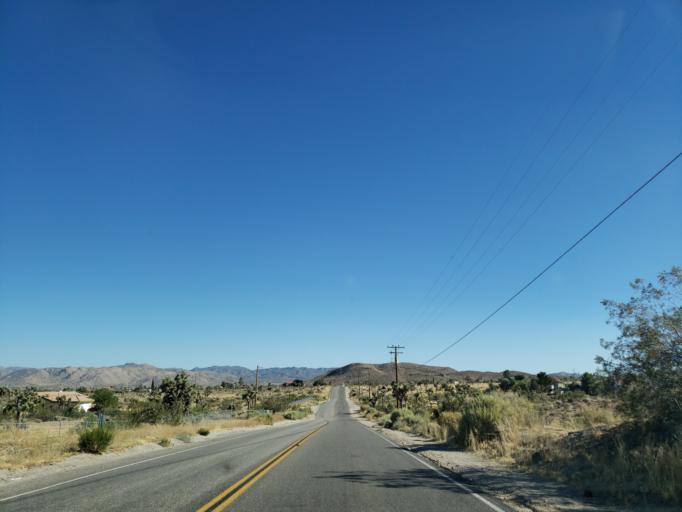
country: US
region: California
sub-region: San Bernardino County
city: Yucca Valley
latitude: 34.1756
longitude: -116.3871
